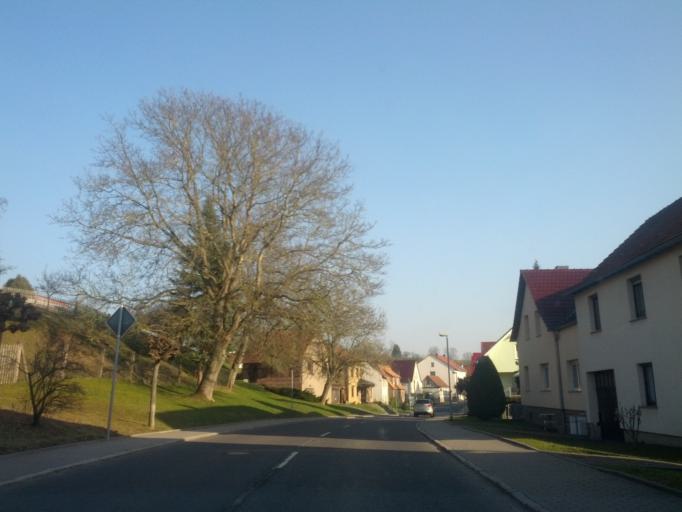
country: DE
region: Thuringia
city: Lauterbach
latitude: 51.0711
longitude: 10.3497
